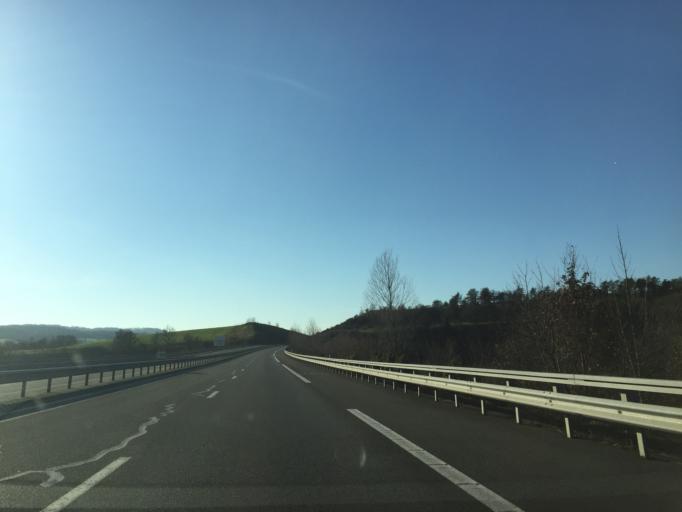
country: FR
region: Aquitaine
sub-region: Departement de la Dordogne
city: Thenon
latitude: 45.1566
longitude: 1.1446
